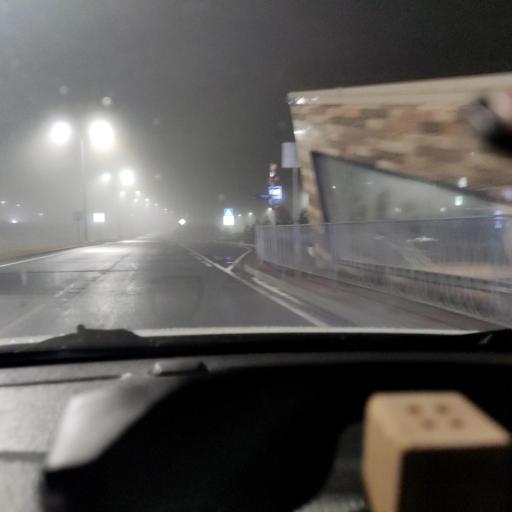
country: RU
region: Tatarstan
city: Sviyazhsk
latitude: 55.7496
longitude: 48.7421
